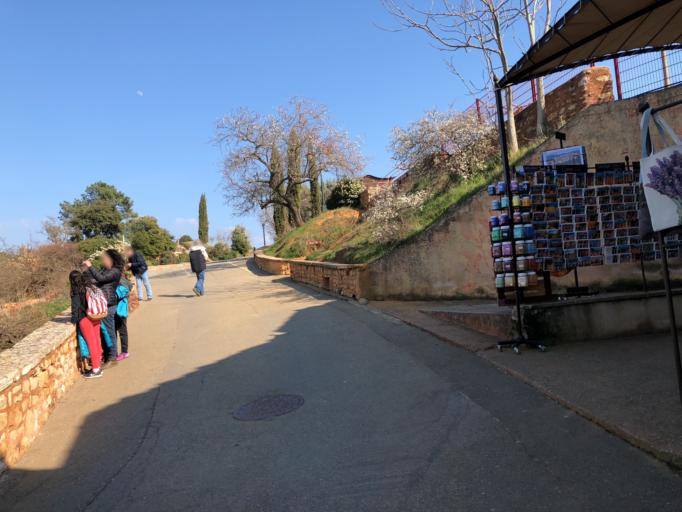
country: FR
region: Provence-Alpes-Cote d'Azur
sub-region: Departement du Vaucluse
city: Roussillon
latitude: 43.9016
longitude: 5.2943
